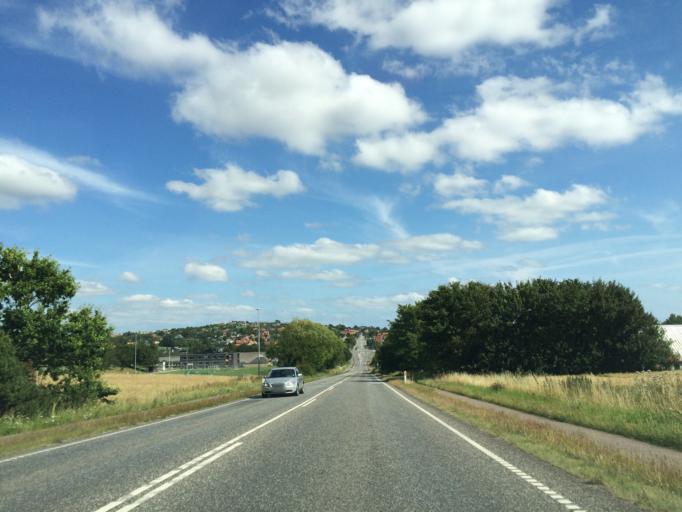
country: DK
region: Central Jutland
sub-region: Syddjurs Kommune
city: Ronde
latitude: 56.3050
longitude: 10.4550
